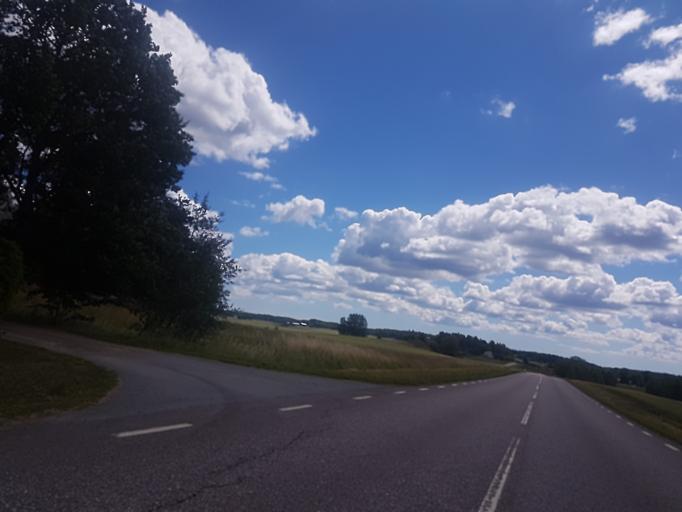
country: SE
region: Soedermanland
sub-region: Gnesta Kommun
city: Gnesta
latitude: 59.0279
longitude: 17.3580
